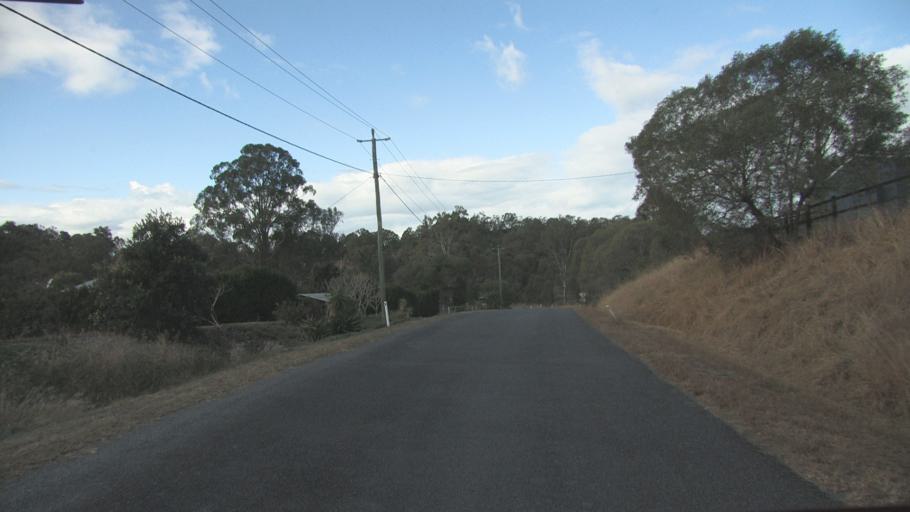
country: AU
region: Queensland
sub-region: Logan
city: Cedar Vale
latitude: -27.9026
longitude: 153.0671
